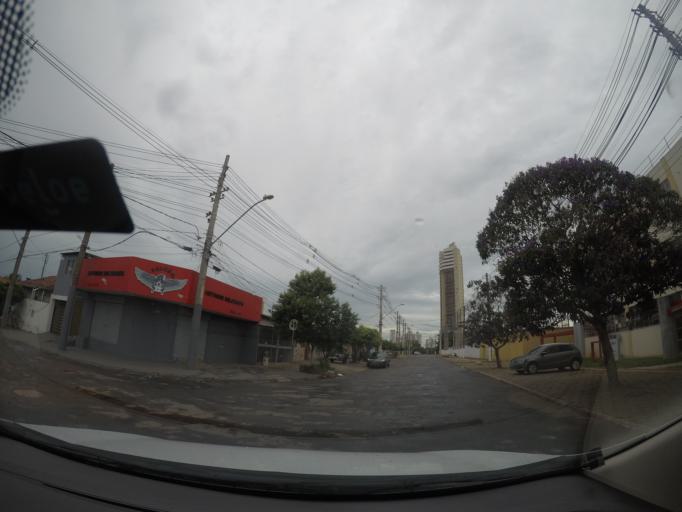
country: BR
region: Goias
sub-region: Goiania
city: Goiania
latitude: -16.6847
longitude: -49.2363
